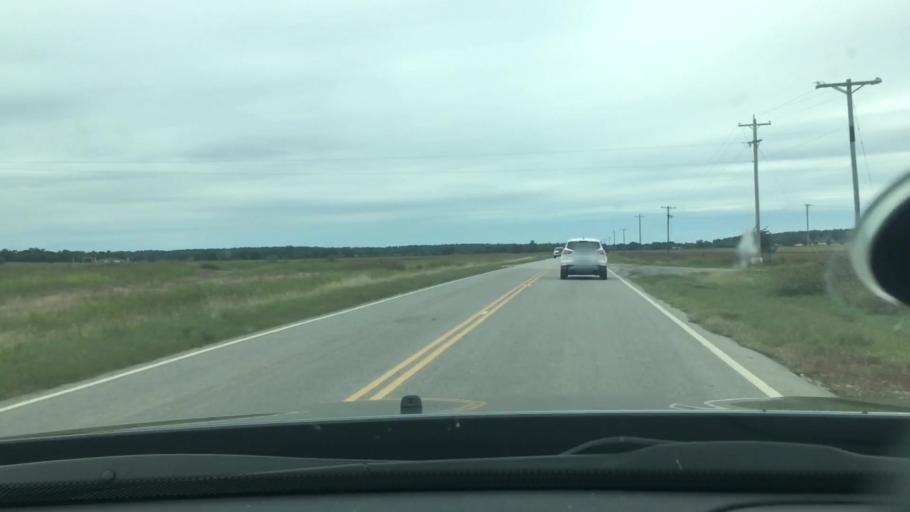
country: US
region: Oklahoma
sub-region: Johnston County
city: Tishomingo
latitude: 34.3379
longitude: -96.4206
